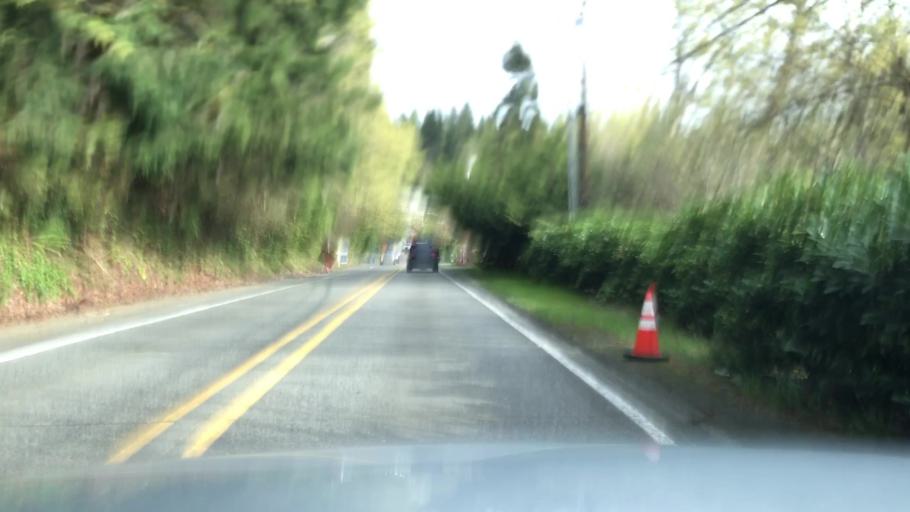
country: US
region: Washington
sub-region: King County
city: West Lake Sammamish
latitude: 47.6046
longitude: -122.1125
